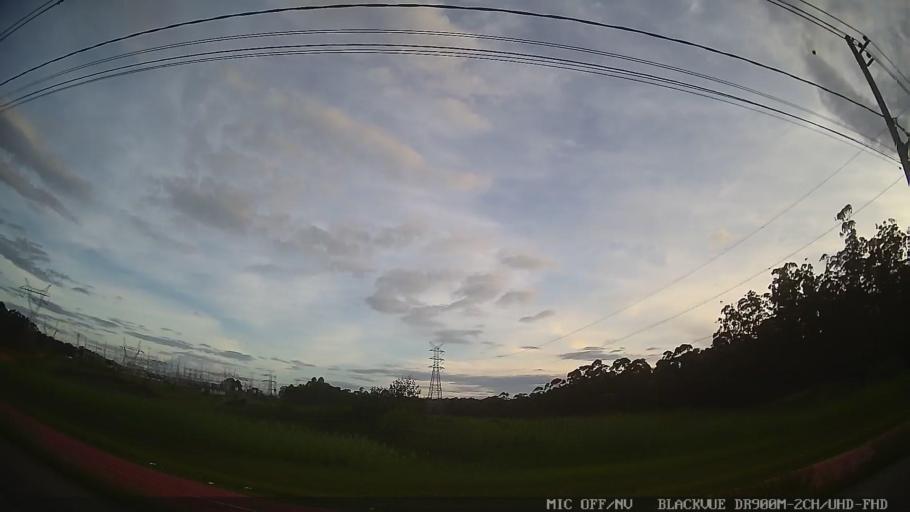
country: BR
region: Sao Paulo
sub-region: Mogi das Cruzes
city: Mogi das Cruzes
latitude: -23.5004
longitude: -46.1736
